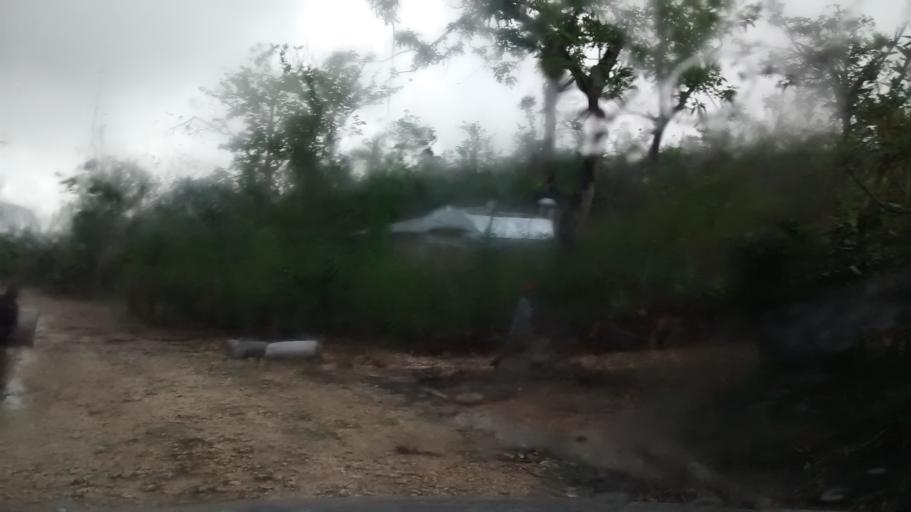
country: HT
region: Grandans
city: Corail
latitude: 18.5321
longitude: -73.9538
